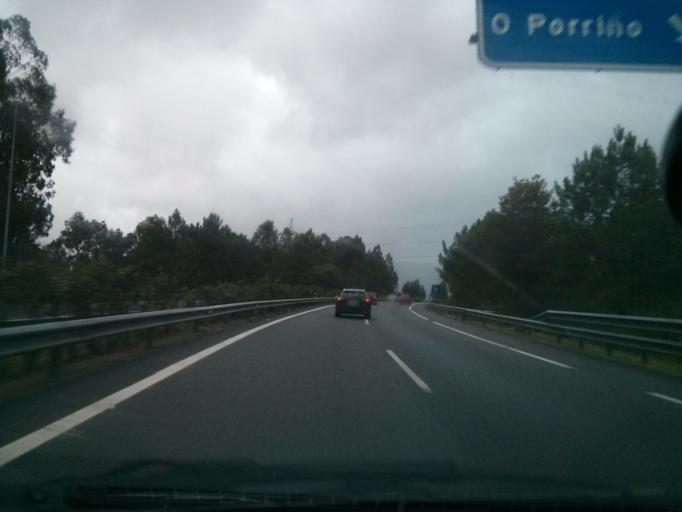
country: ES
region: Galicia
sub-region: Provincia de Pontevedra
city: Porrino
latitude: 42.1607
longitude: -8.6009
